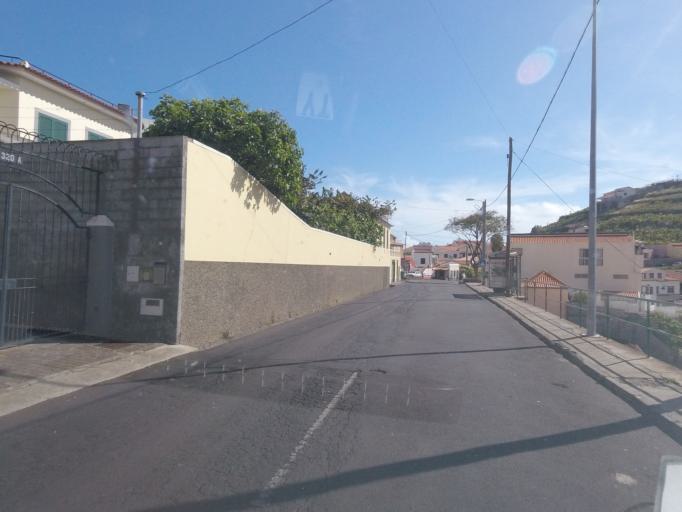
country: PT
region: Madeira
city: Camara de Lobos
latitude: 32.6545
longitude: -16.9706
